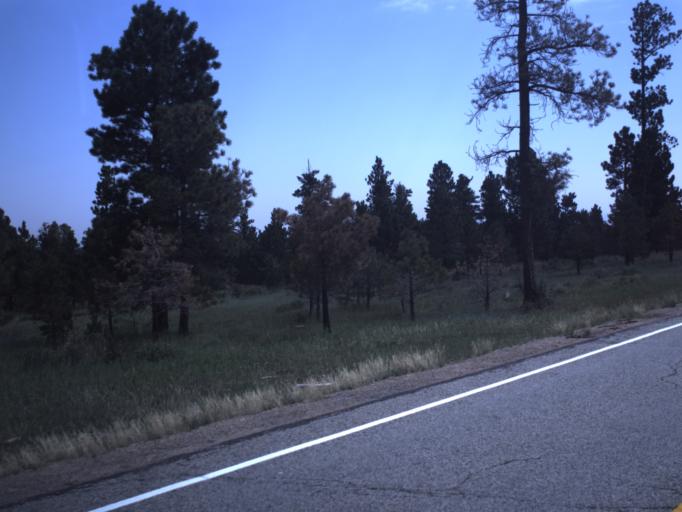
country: US
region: Utah
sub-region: Daggett County
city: Manila
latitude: 40.8589
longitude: -109.5538
